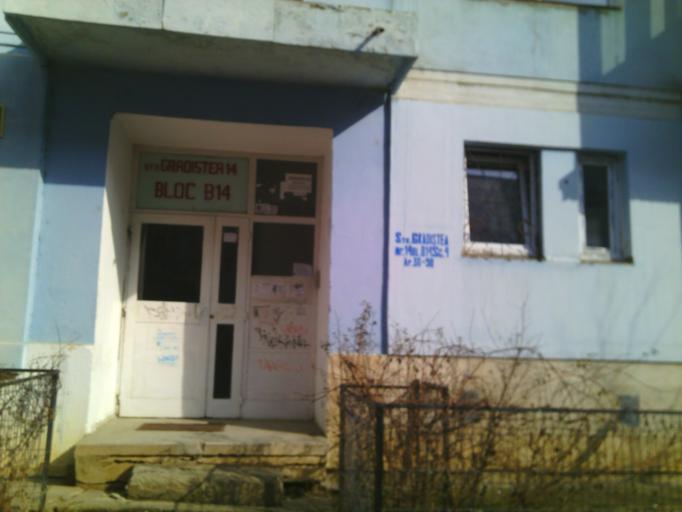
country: RO
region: Bucuresti
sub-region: Municipiul Bucuresti
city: Bucuresti
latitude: 44.3835
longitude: 26.0979
